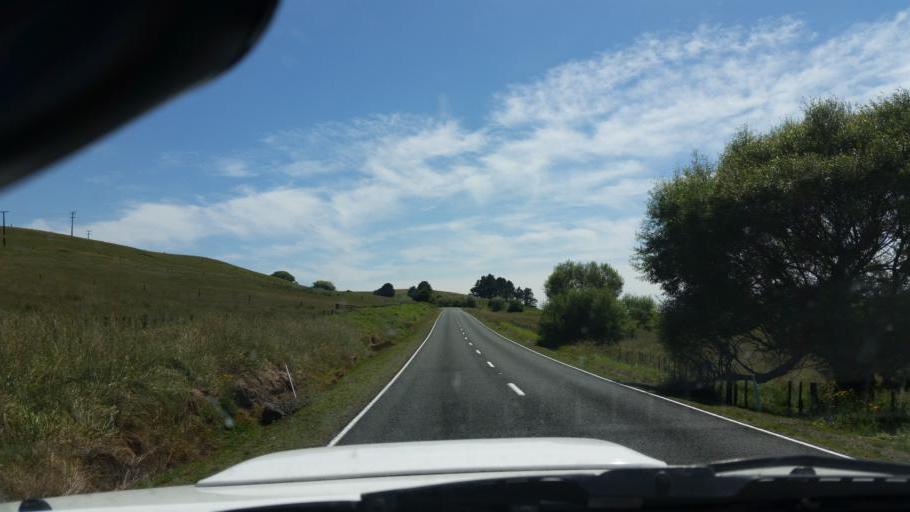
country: NZ
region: Auckland
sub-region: Auckland
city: Wellsford
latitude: -36.1873
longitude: 174.4095
